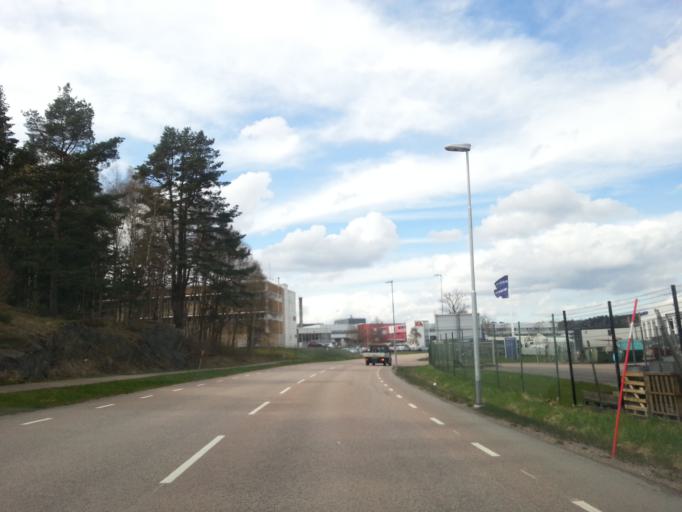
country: SE
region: Vaestra Goetaland
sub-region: Kungalvs Kommun
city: Kungalv
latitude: 57.8719
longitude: 11.9332
